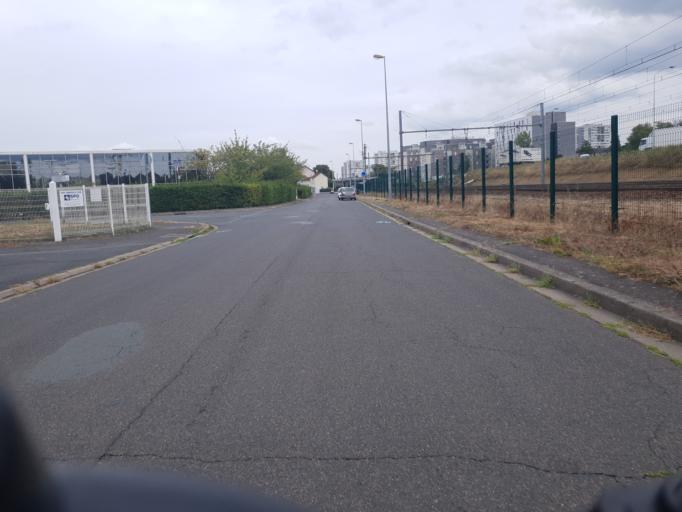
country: FR
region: Centre
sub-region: Departement d'Indre-et-Loire
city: Tours
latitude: 47.3768
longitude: 0.6752
